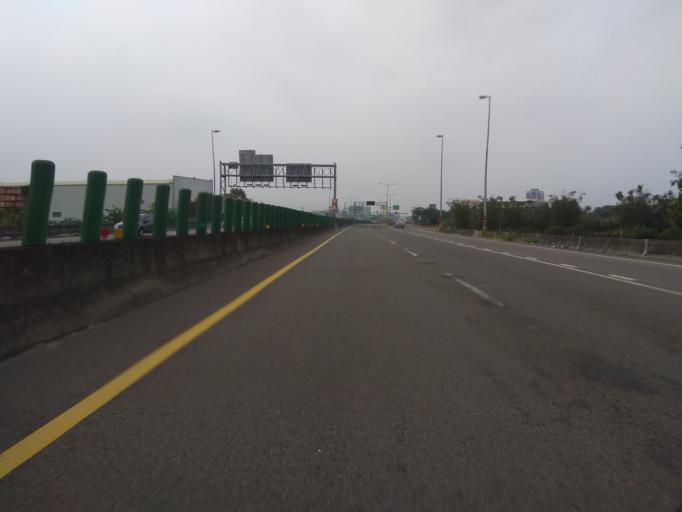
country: TW
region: Taiwan
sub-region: Miaoli
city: Miaoli
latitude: 24.6997
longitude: 120.8657
